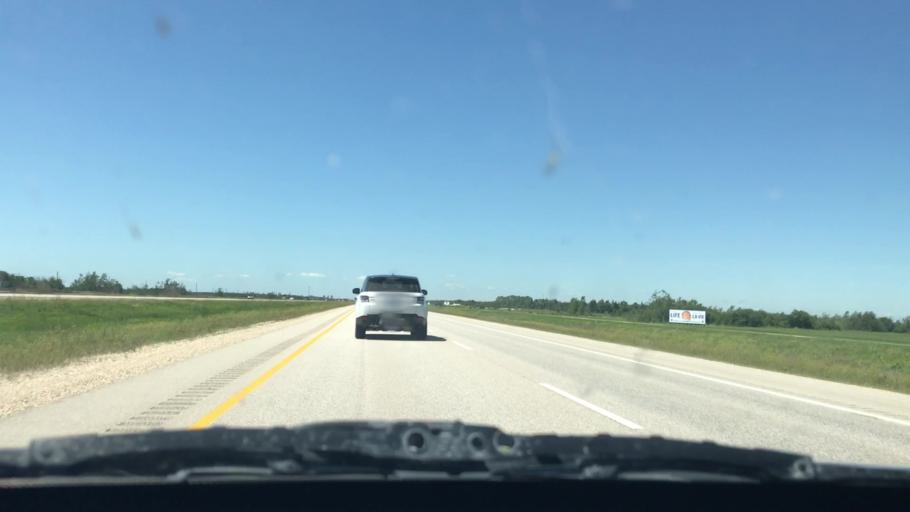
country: CA
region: Manitoba
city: Niverville
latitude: 49.8052
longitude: -96.8993
